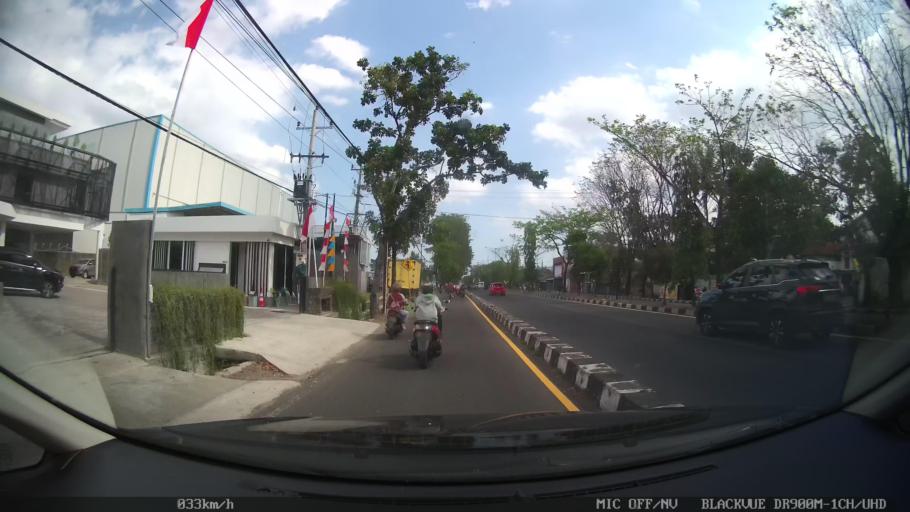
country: ID
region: Daerah Istimewa Yogyakarta
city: Yogyakarta
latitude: -7.7661
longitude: 110.3354
